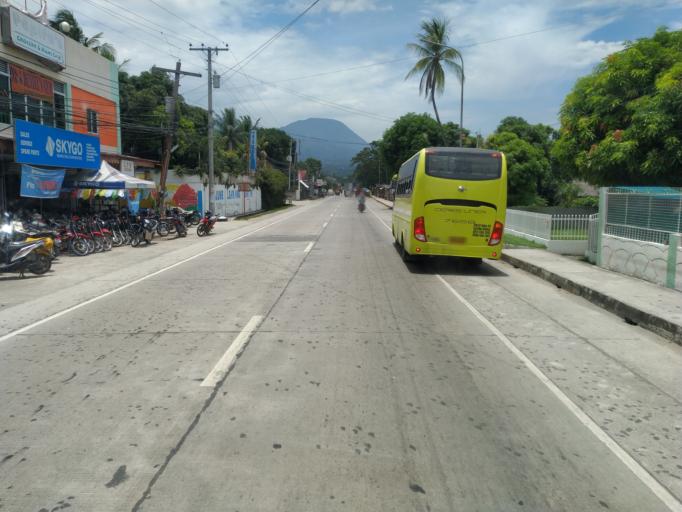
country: PH
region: Central Visayas
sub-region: Province of Negros Oriental
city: Sibulan
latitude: 9.3598
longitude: 123.2831
